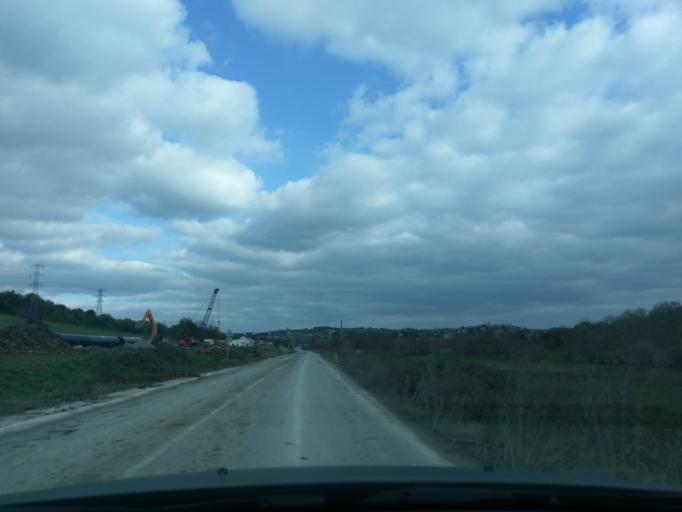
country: TR
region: Istanbul
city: Durusu
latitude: 41.2909
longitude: 28.6648
